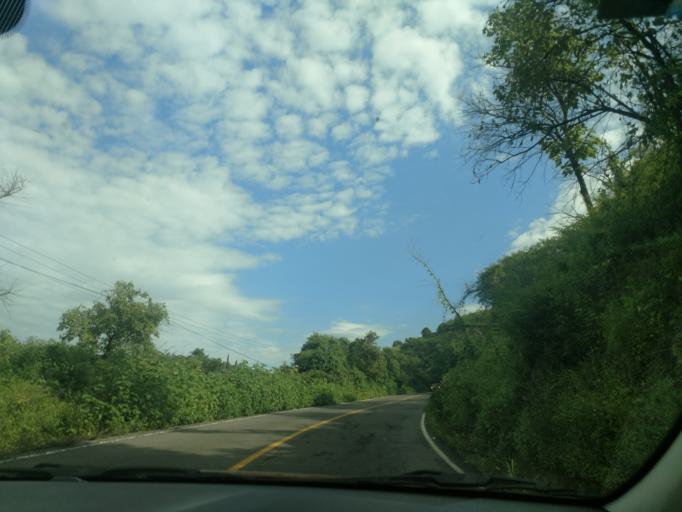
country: MX
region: Jalisco
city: Ameca
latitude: 20.5352
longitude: -104.1903
